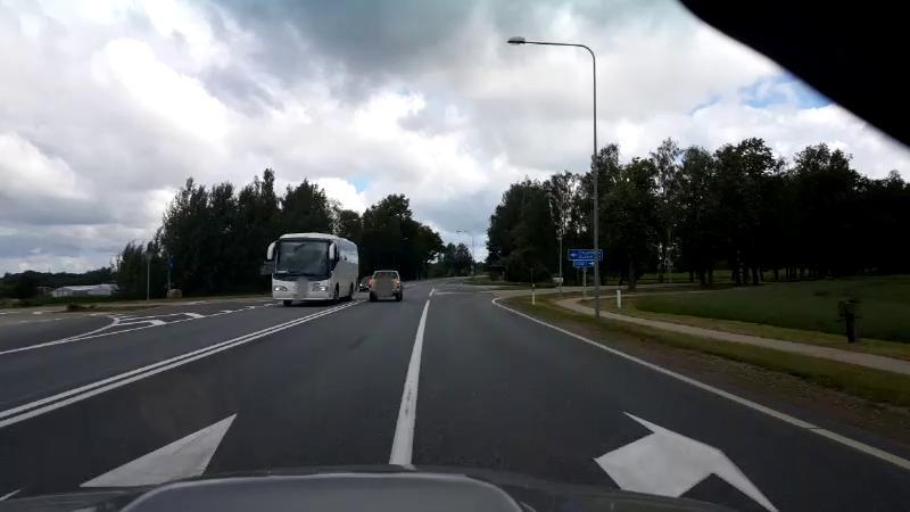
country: LV
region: Bauskas Rajons
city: Bauska
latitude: 56.4670
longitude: 24.1635
